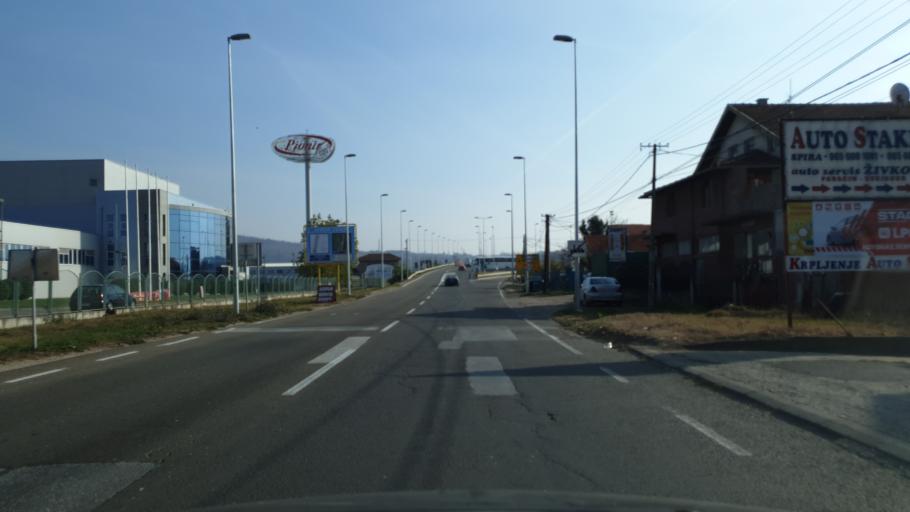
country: RS
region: Central Serbia
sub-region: Pomoravski Okrug
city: Paracin
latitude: 43.8580
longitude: 21.4314
